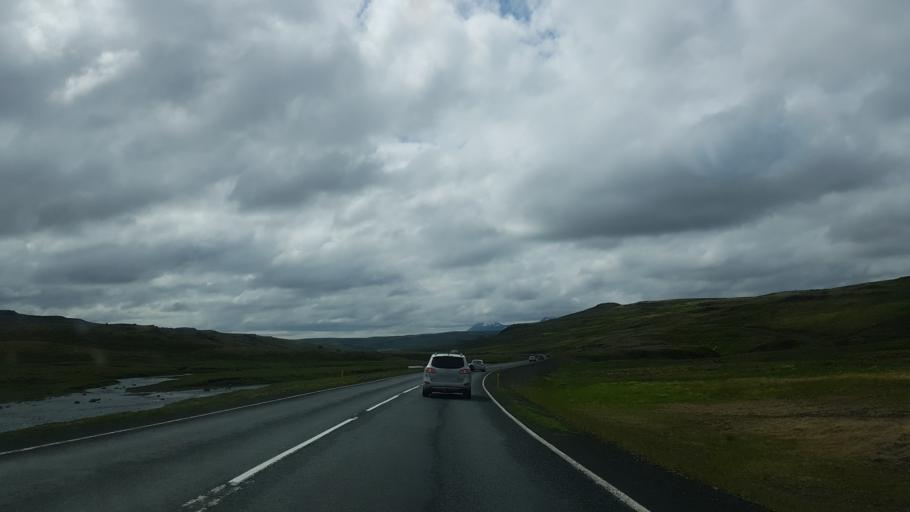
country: IS
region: West
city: Borgarnes
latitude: 64.9253
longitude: -21.1081
